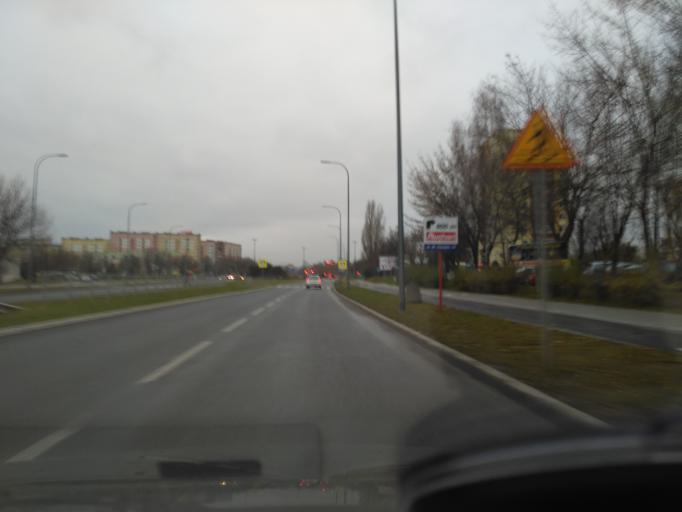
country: PL
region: Lublin Voivodeship
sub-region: Powiat lubelski
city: Lublin
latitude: 51.2602
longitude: 22.5530
